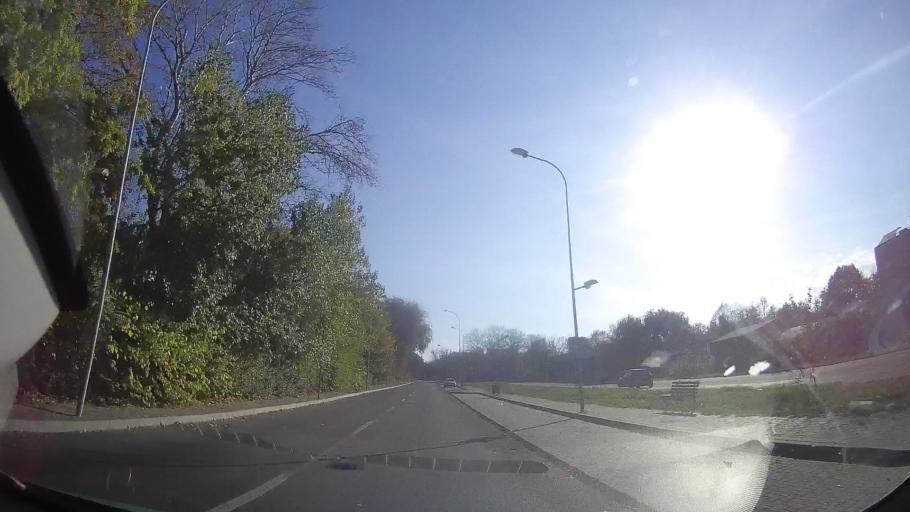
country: RO
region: Constanta
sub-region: Comuna Douazeci si Trei August
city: Douazeci si Trei August
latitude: 43.8624
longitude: 28.5979
